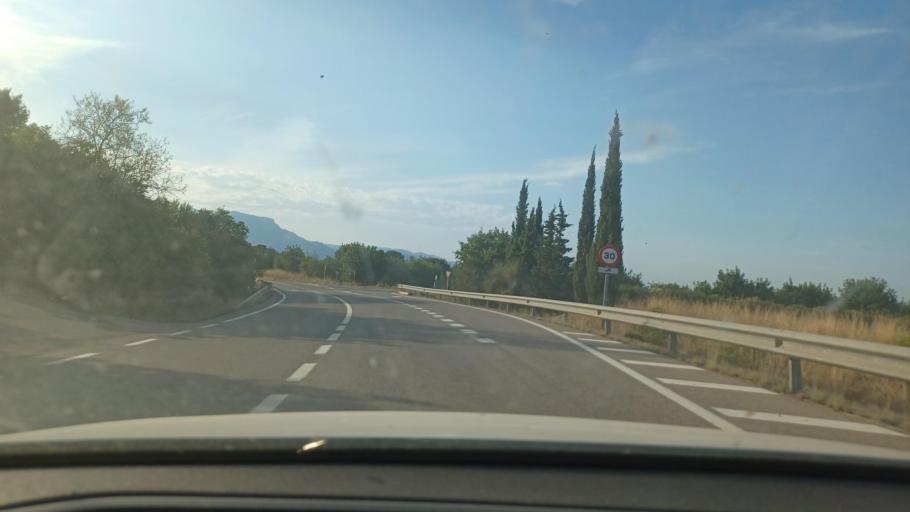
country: ES
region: Catalonia
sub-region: Provincia de Tarragona
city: Santa Barbara
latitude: 40.7131
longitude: 0.4843
